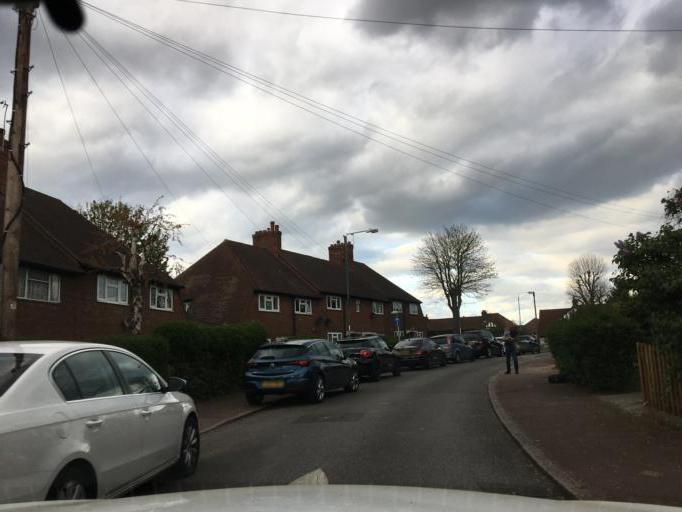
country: GB
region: England
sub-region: Greater London
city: Blackheath
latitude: 51.4477
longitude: 0.0356
